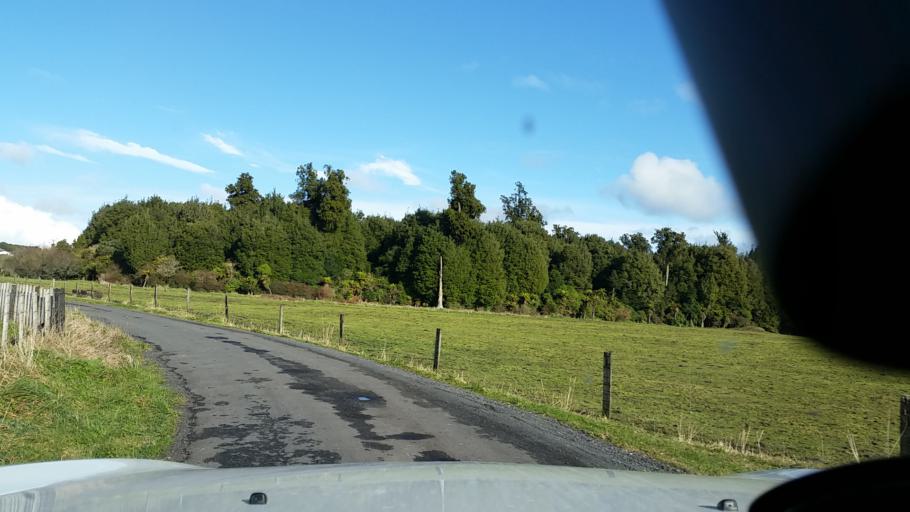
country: NZ
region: Bay of Plenty
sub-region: Rotorua District
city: Rotorua
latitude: -38.0981
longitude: 176.0738
